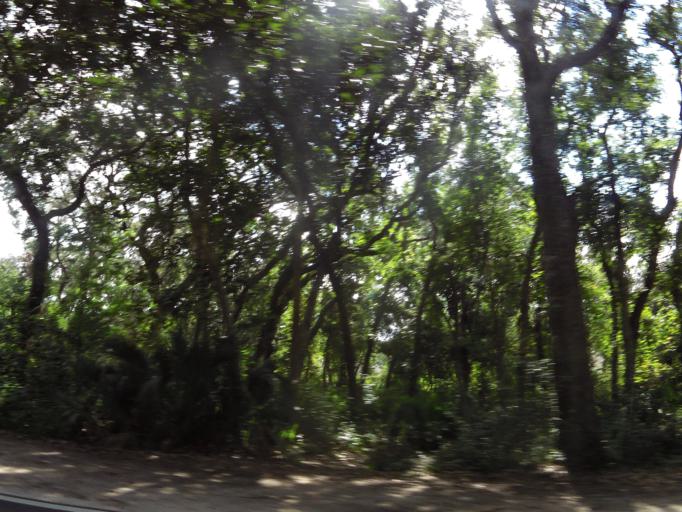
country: US
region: Florida
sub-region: Nassau County
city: Fernandina Beach
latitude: 30.5818
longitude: -81.4468
